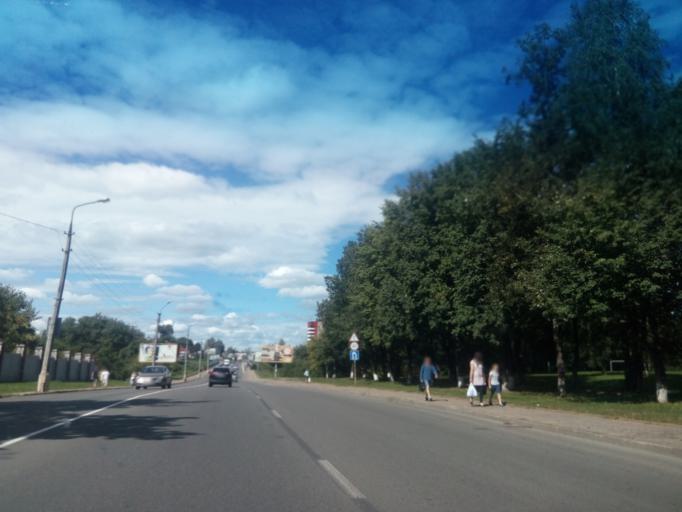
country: BY
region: Vitebsk
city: Polatsk
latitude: 55.4927
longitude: 28.7745
